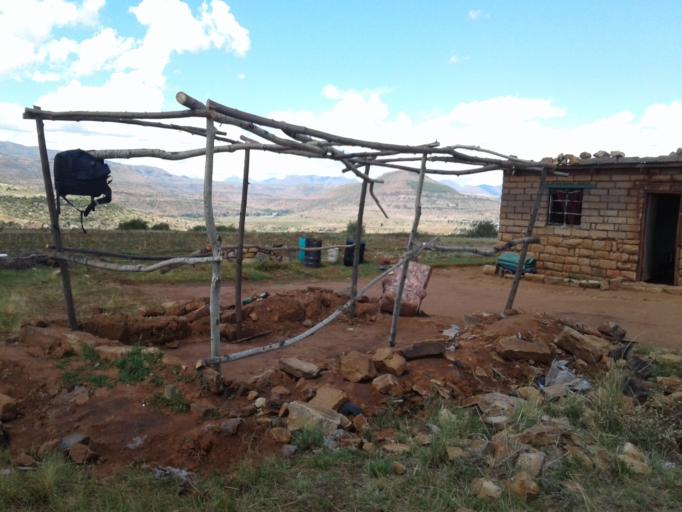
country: LS
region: Quthing
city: Quthing
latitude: -30.3741
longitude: 27.5546
